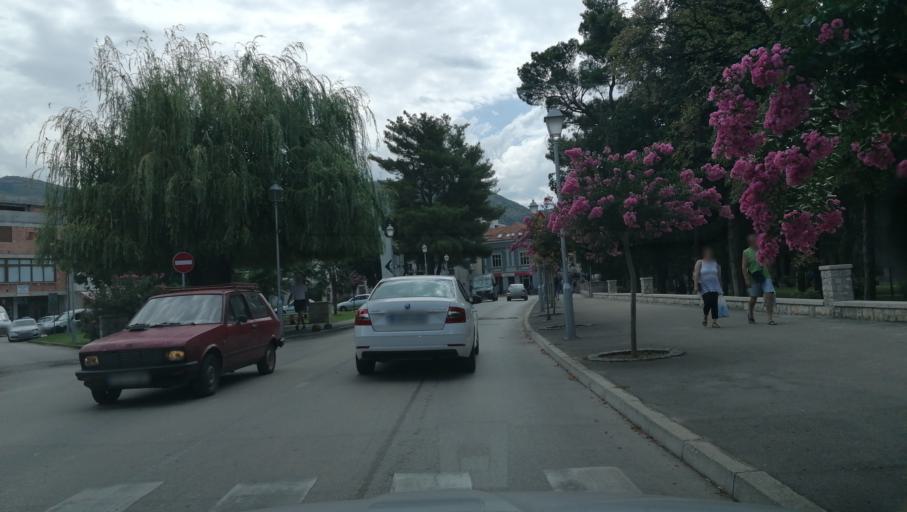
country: BA
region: Republika Srpska
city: Trebinje
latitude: 42.7105
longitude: 18.3456
